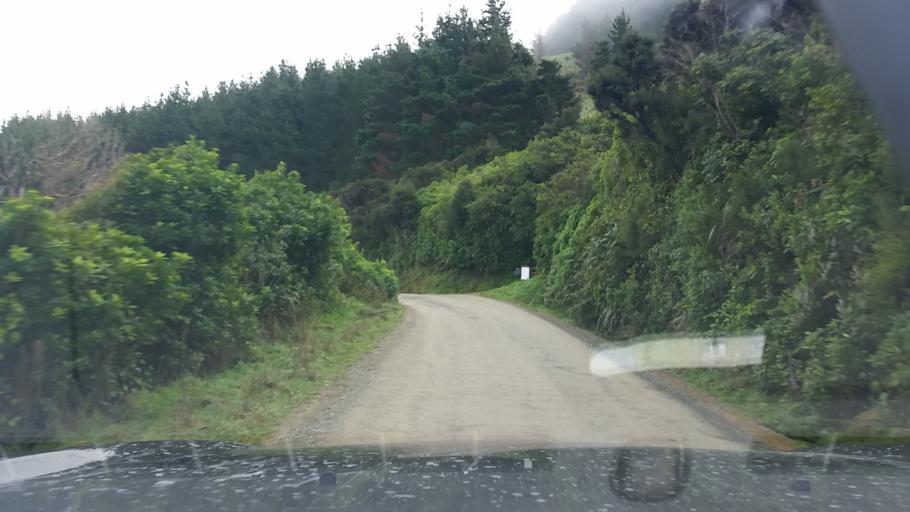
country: NZ
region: Marlborough
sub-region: Marlborough District
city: Picton
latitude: -41.1753
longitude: 174.0451
